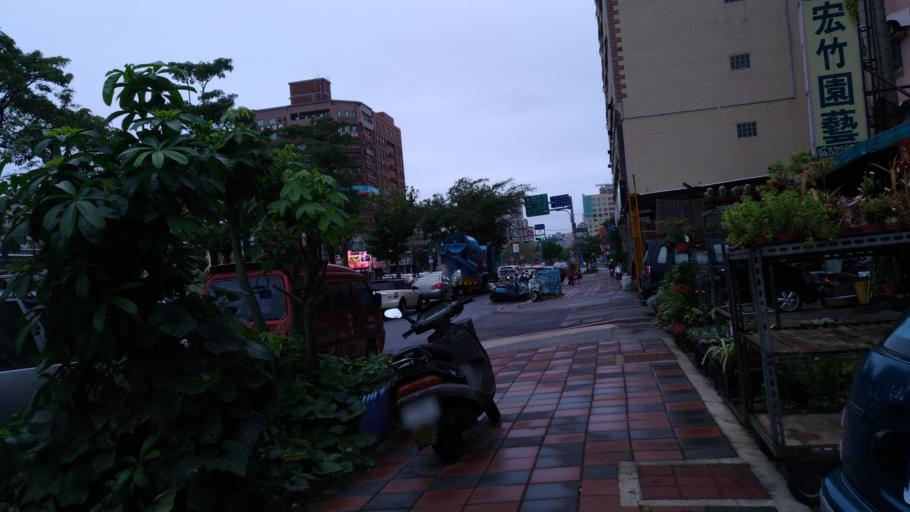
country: TW
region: Taiwan
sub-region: Hsinchu
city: Hsinchu
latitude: 24.8102
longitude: 120.9708
